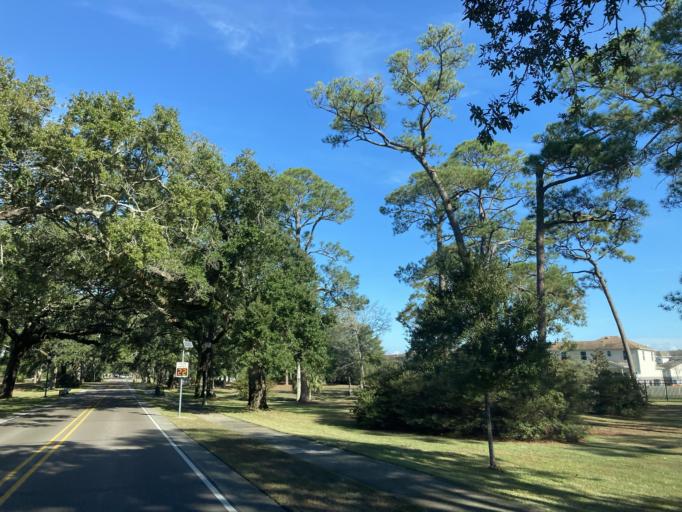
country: US
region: Mississippi
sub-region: Harrison County
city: D'Iberville
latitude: 30.4059
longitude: -88.9472
